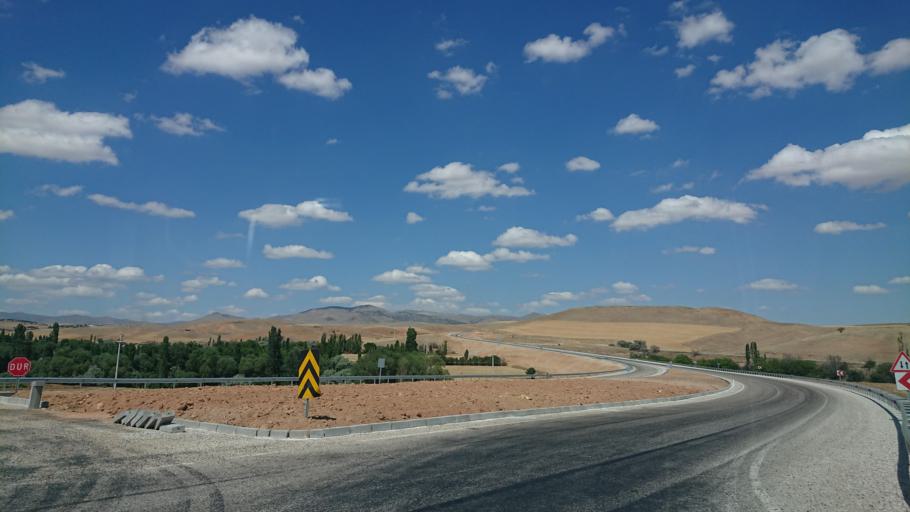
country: TR
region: Ankara
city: Evren
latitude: 39.1015
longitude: 33.9065
